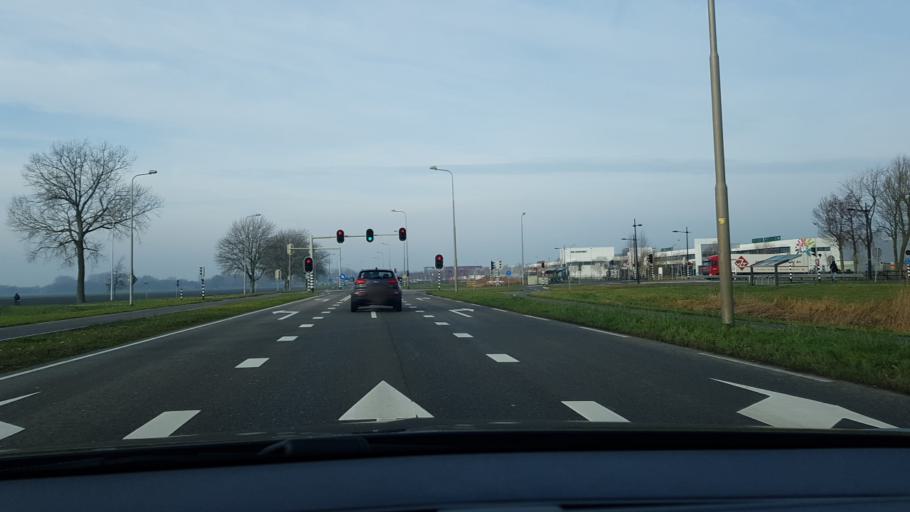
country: NL
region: North Holland
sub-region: Gemeente Aalsmeer
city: Aalsmeer
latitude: 52.2508
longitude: 4.7938
